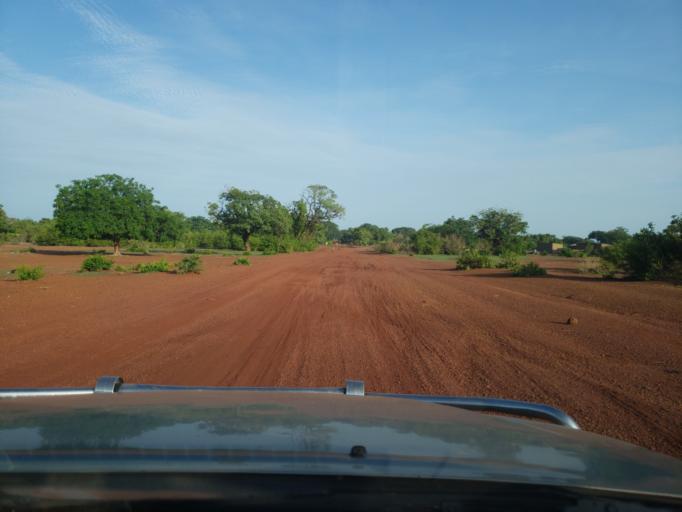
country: ML
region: Sikasso
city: Koutiala
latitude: 12.4201
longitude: -5.5811
